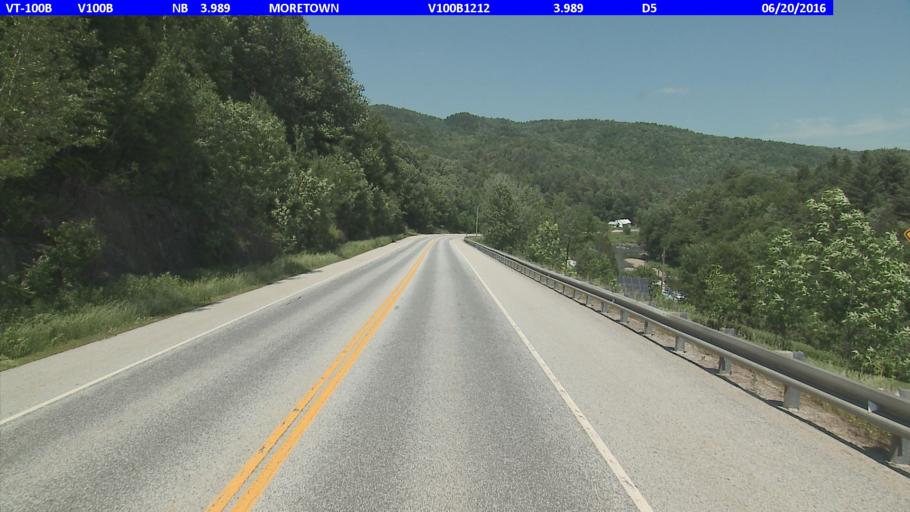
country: US
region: Vermont
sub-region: Washington County
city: Waterbury
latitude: 44.2835
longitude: -72.7346
